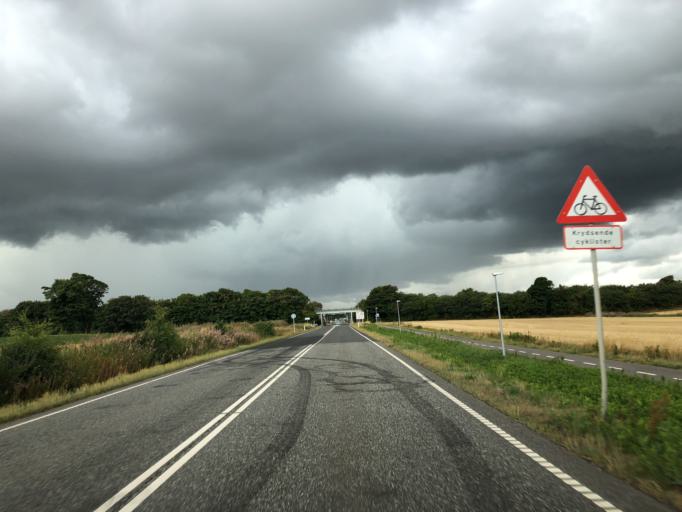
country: DK
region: Central Jutland
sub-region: Ikast-Brande Kommune
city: Bording Kirkeby
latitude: 56.1372
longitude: 9.3556
